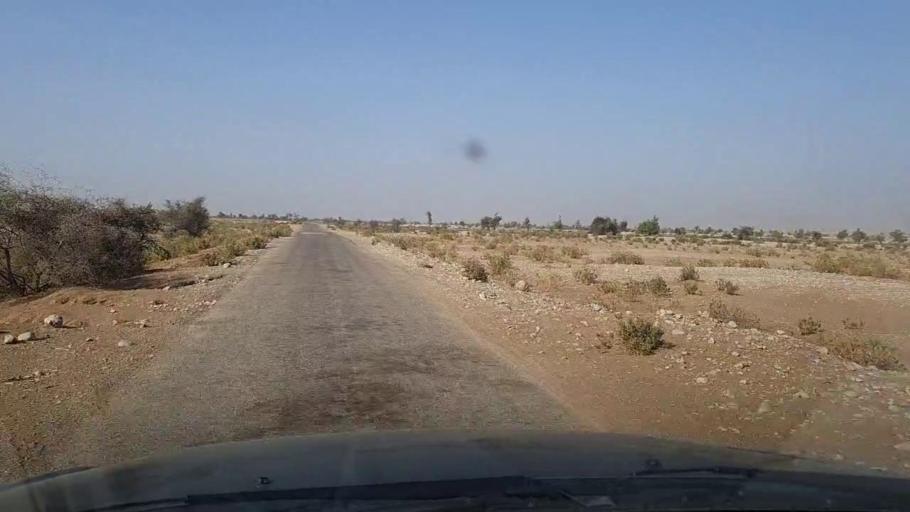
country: PK
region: Sindh
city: Sann
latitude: 25.9318
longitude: 68.0227
